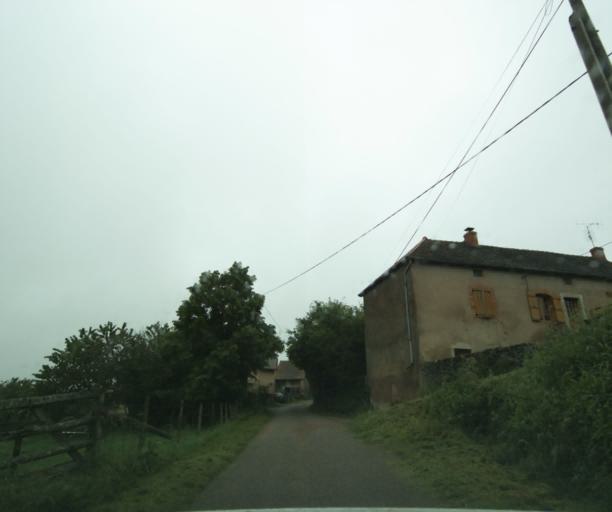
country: FR
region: Bourgogne
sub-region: Departement de Saone-et-Loire
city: Charolles
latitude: 46.4105
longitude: 4.3877
